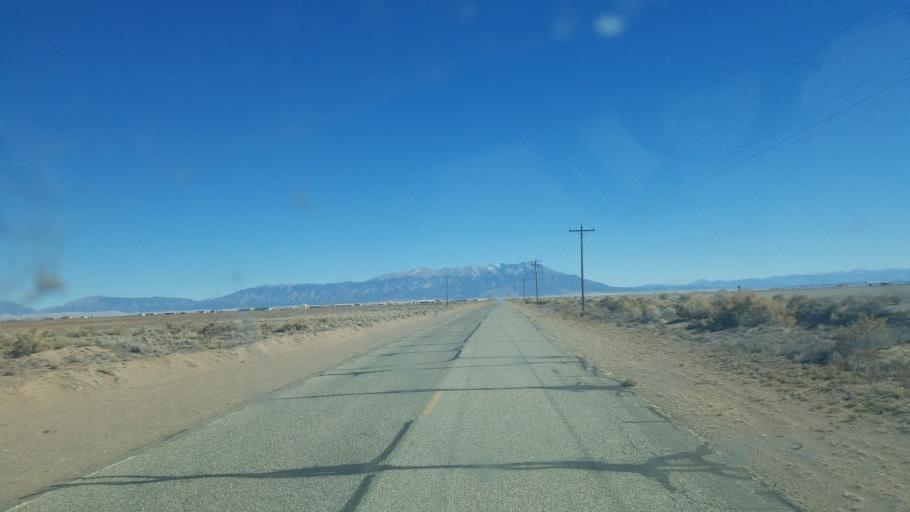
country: US
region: Colorado
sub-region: Alamosa County
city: Alamosa
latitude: 37.5745
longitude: -105.9185
